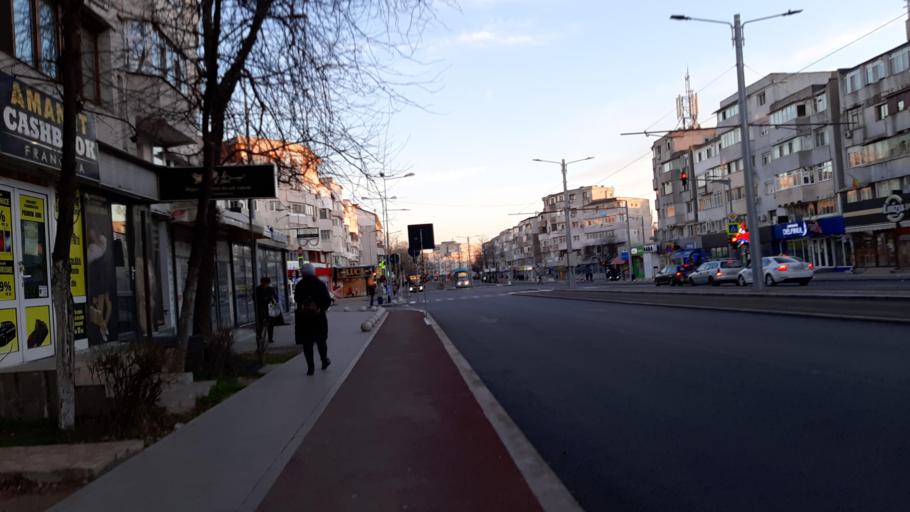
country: RO
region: Galati
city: Galati
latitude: 45.4373
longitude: 28.0233
